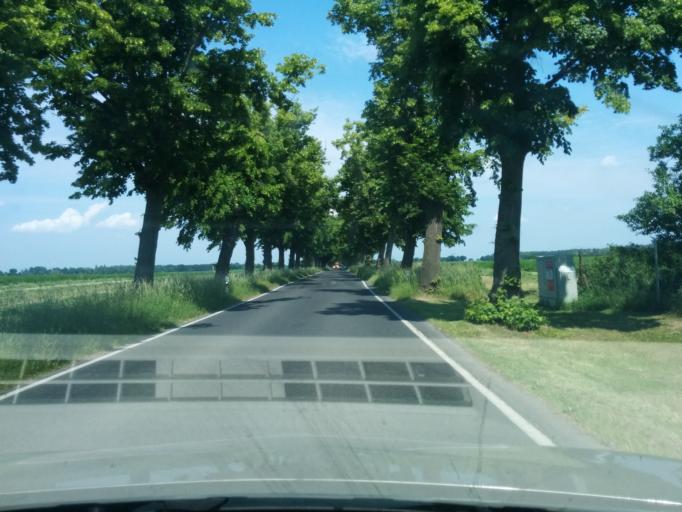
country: DE
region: Brandenburg
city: Bernau bei Berlin
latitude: 52.6326
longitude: 13.5746
